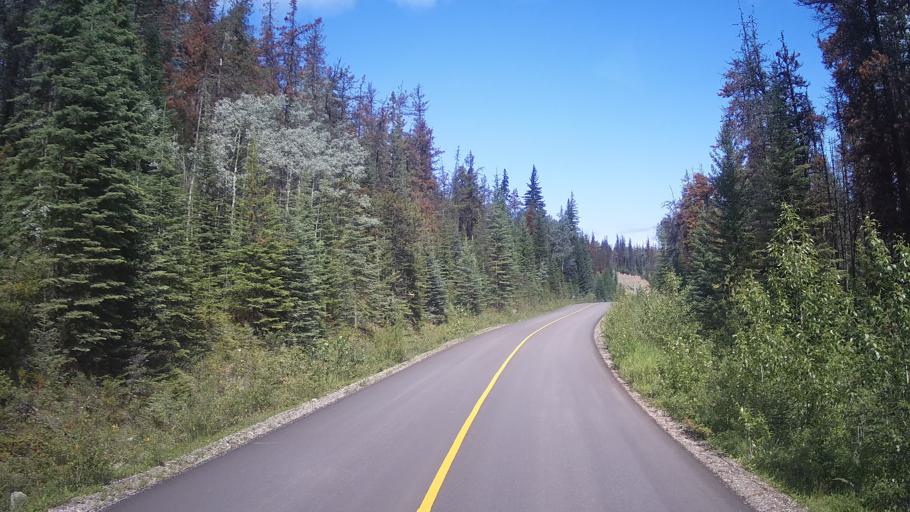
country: CA
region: Alberta
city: Jasper Park Lodge
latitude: 52.6637
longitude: -117.8875
